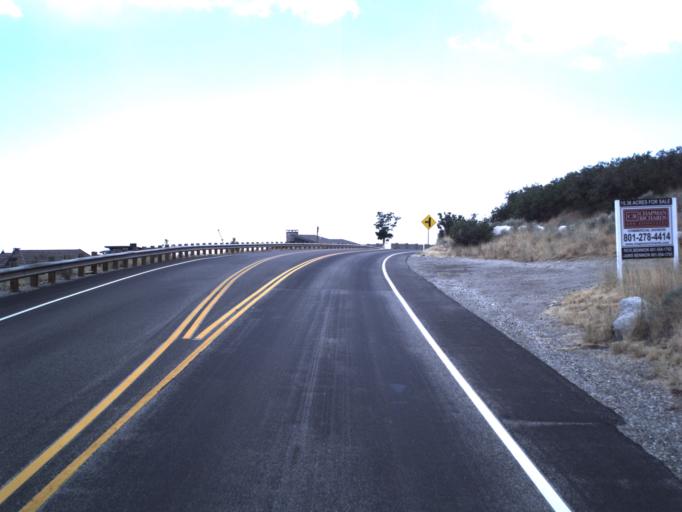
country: US
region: Utah
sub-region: Salt Lake County
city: Granite
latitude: 40.5796
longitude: -111.7914
